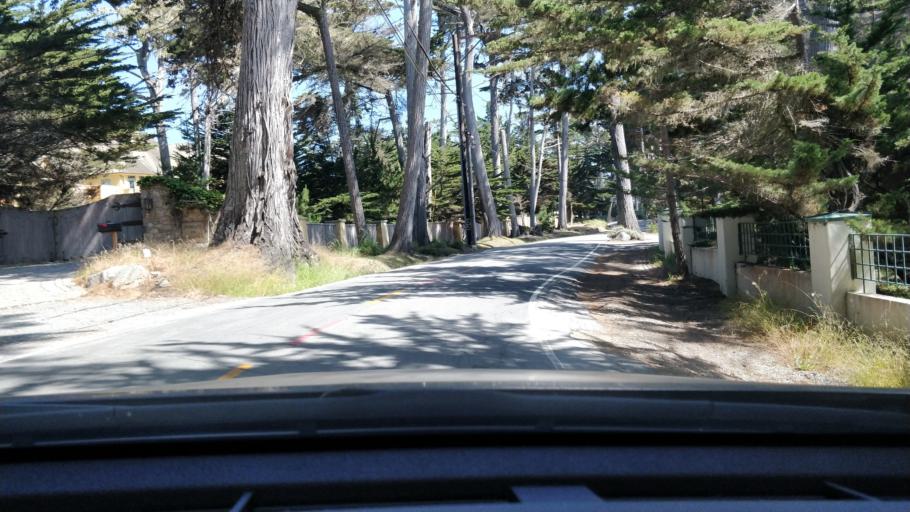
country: US
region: California
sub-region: Monterey County
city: Del Monte Forest
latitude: 36.5721
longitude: -121.9694
